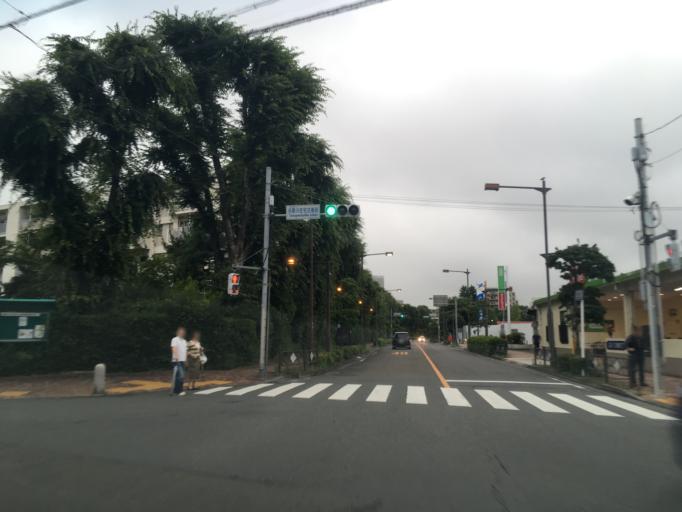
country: JP
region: Tokyo
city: Chofugaoka
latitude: 35.6396
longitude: 139.5597
